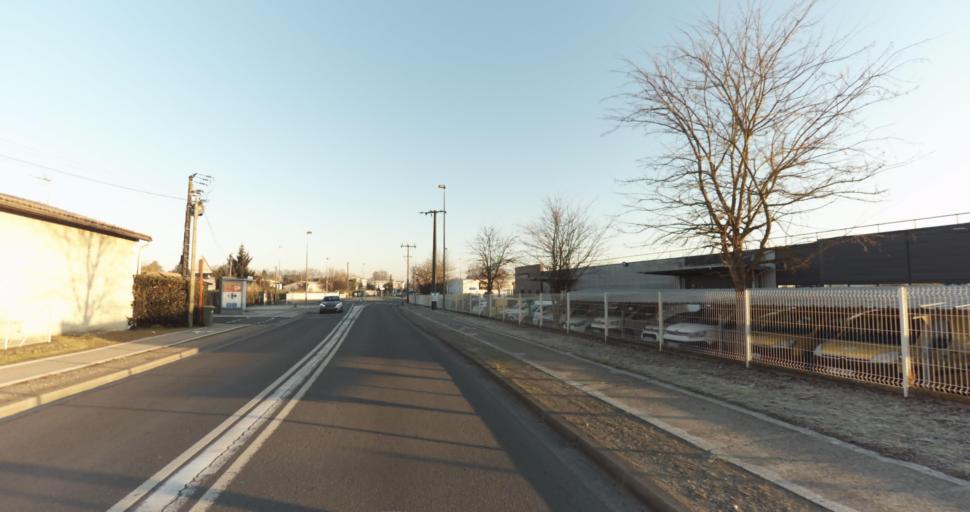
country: FR
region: Aquitaine
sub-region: Departement de la Gironde
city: Ambares-et-Lagrave
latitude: 44.9125
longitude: -0.4939
